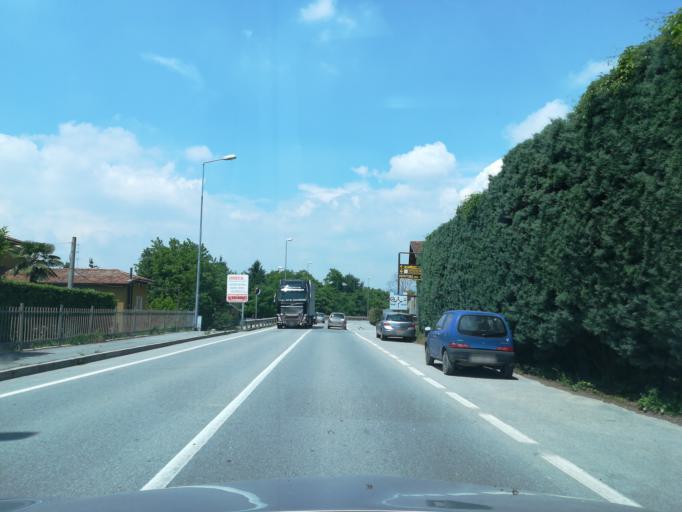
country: IT
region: Lombardy
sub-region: Provincia di Bergamo
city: Grassobbio
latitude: 45.6587
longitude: 9.7437
